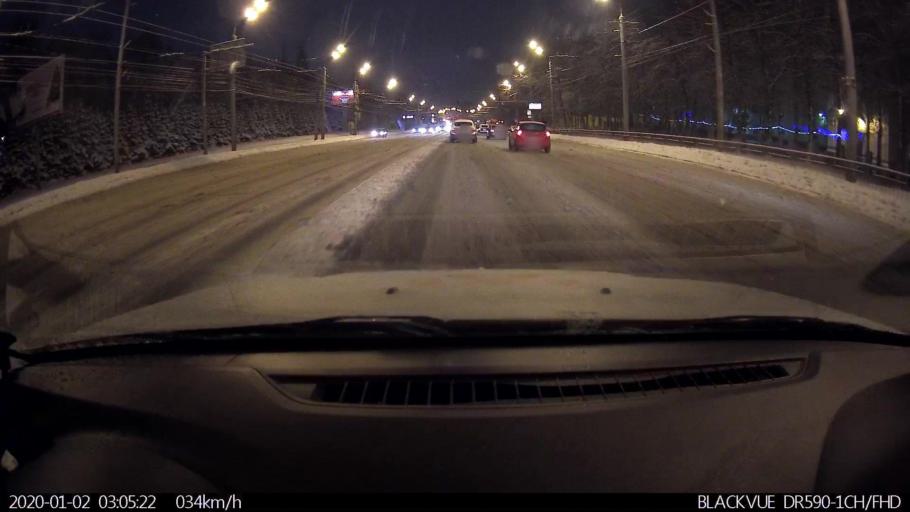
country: RU
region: Nizjnij Novgorod
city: Nizhniy Novgorod
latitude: 56.2924
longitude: 43.9843
